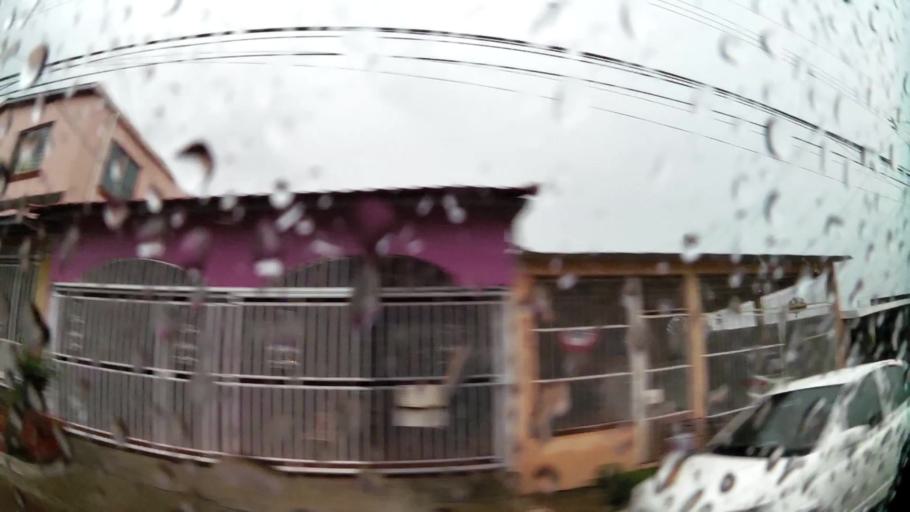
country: PA
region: Panama
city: San Miguelito
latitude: 9.0563
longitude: -79.4754
